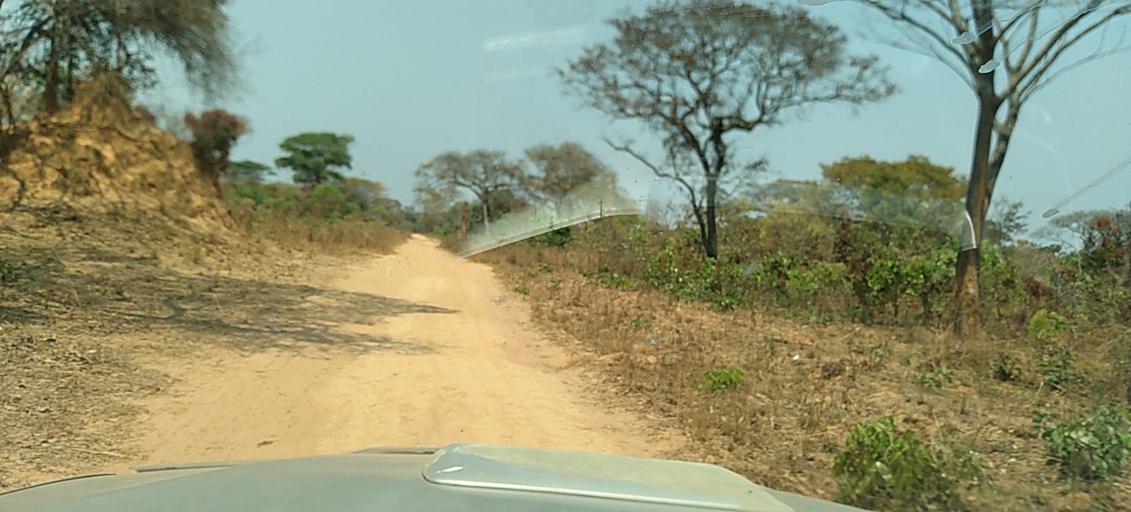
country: ZM
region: North-Western
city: Kasempa
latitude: -13.6540
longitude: 26.2553
